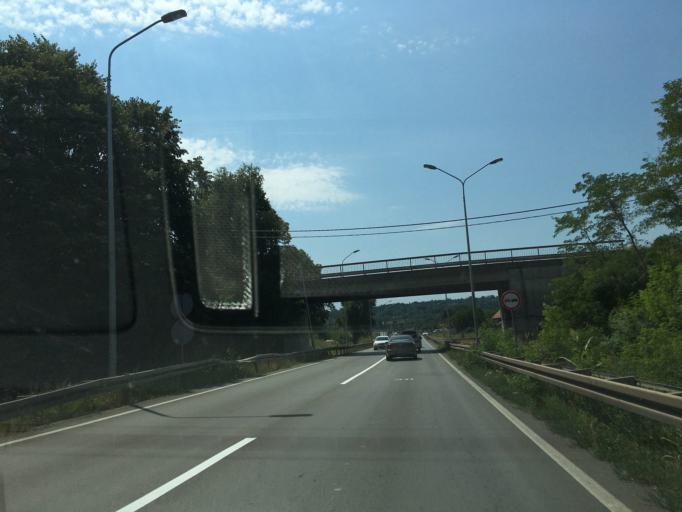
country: RS
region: Central Serbia
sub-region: Podunavski Okrug
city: Smederevo
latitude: 44.5925
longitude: 20.9568
